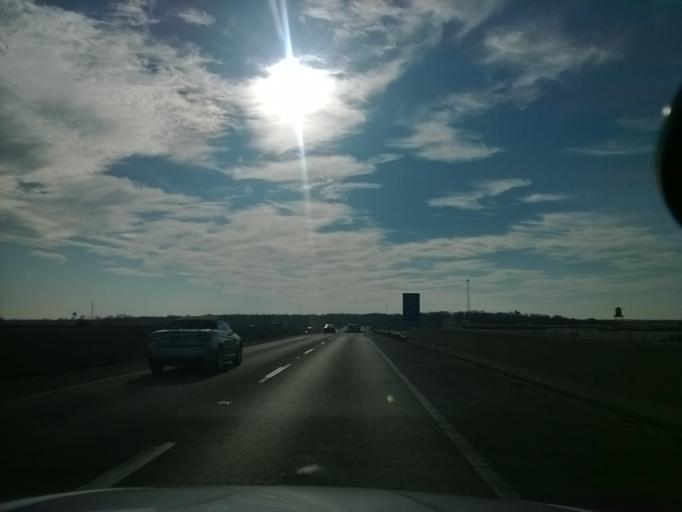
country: US
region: Indiana
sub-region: Johnson County
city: Edinburgh
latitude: 39.3124
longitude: -85.9544
